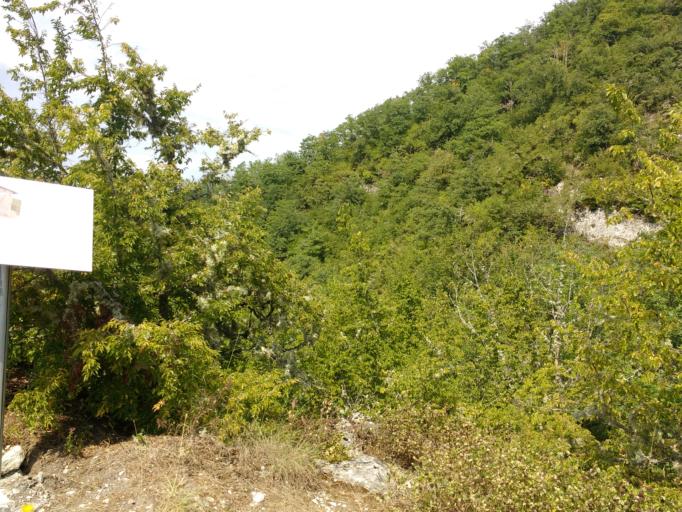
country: GE
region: Racha-Lechkhumi and Kvemo Svaneti
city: Ambrolauri
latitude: 42.5557
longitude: 43.1204
